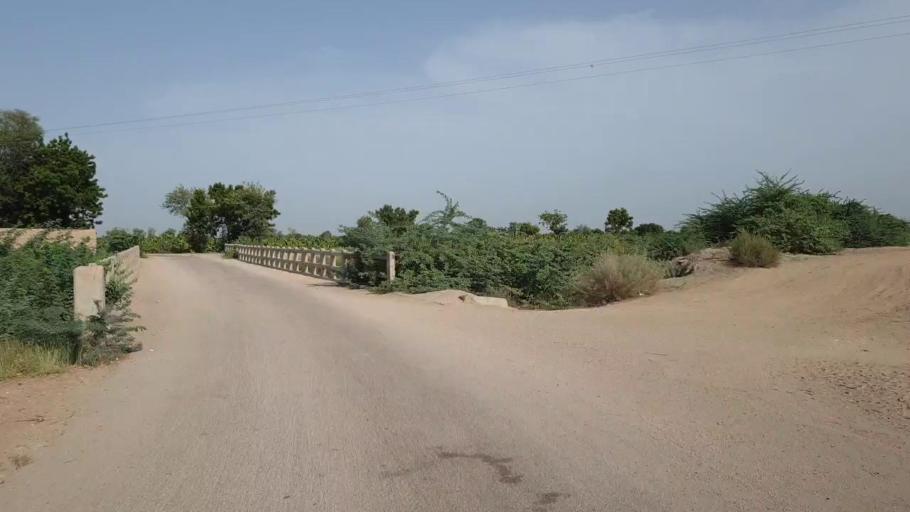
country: PK
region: Sindh
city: Sakrand
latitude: 26.2624
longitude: 68.2816
